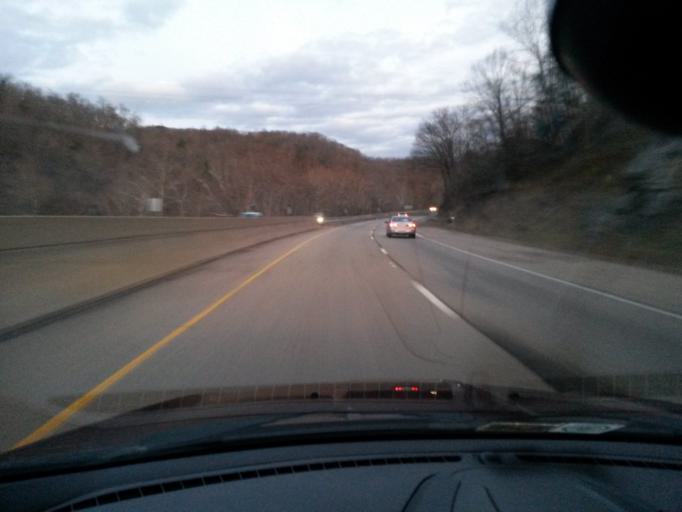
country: US
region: Virginia
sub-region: City of Covington
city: Fairlawn
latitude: 37.7797
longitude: -79.9322
